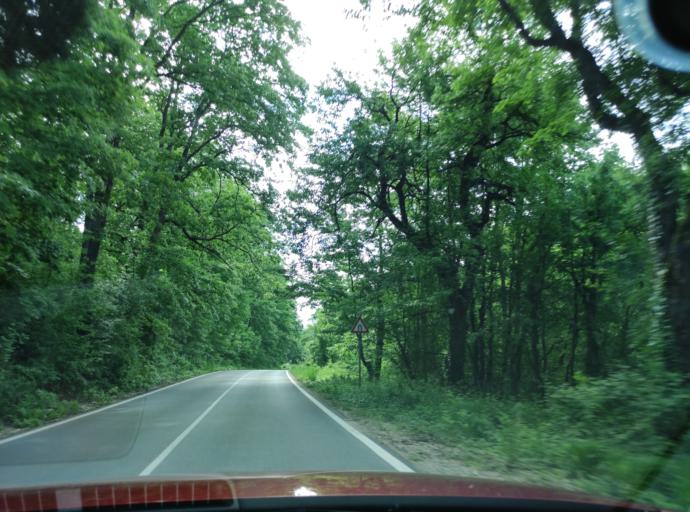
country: BG
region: Montana
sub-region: Obshtina Chiprovtsi
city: Chiprovtsi
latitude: 43.4636
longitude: 22.8863
